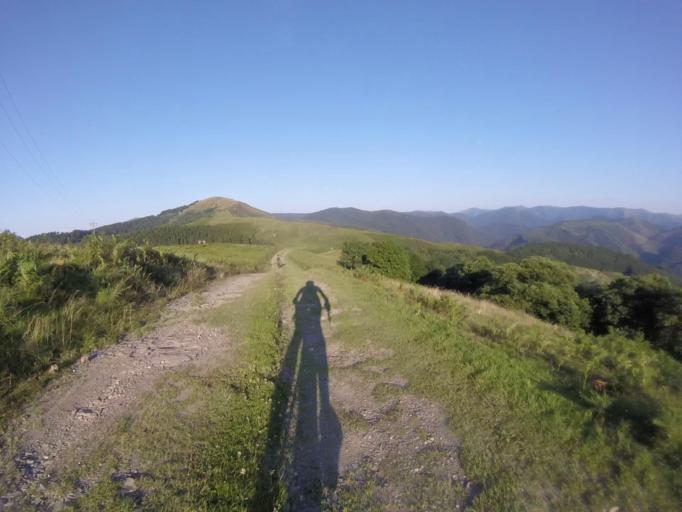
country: ES
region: Navarre
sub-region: Provincia de Navarra
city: Arano
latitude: 43.2425
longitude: -1.8452
